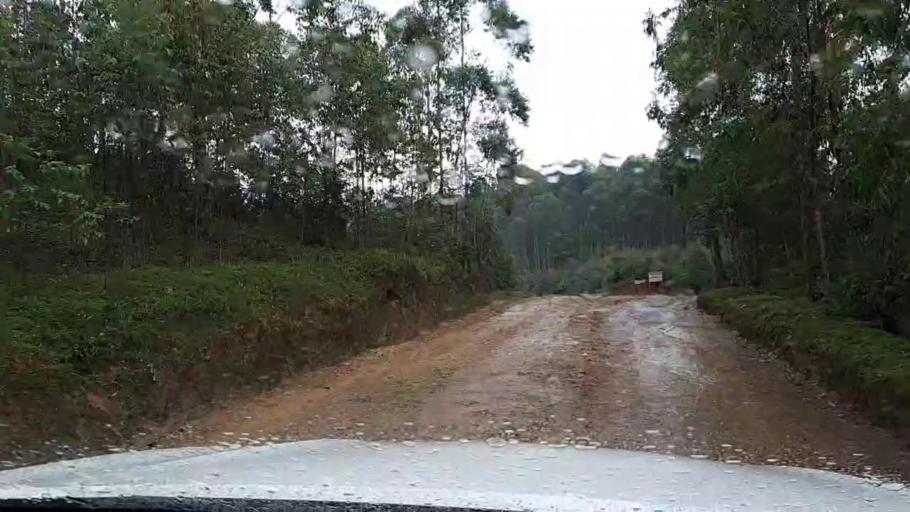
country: RW
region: Western Province
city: Cyangugu
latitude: -2.5497
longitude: 28.9784
